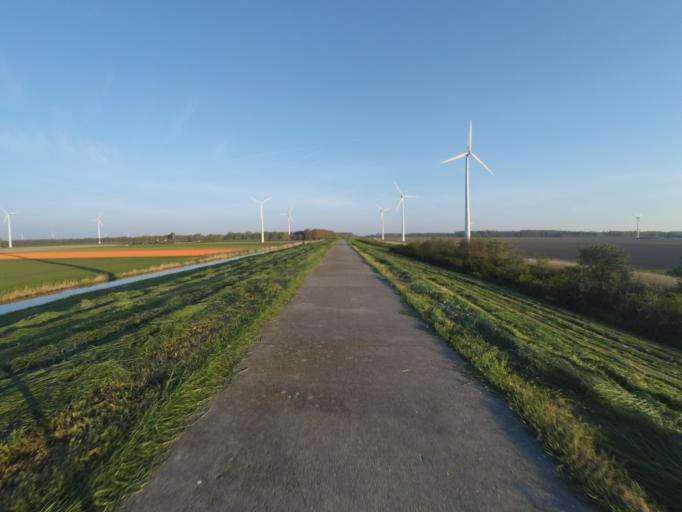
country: NL
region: Flevoland
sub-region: Gemeente Zeewolde
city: Zeewolde
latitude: 52.3953
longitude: 5.5145
